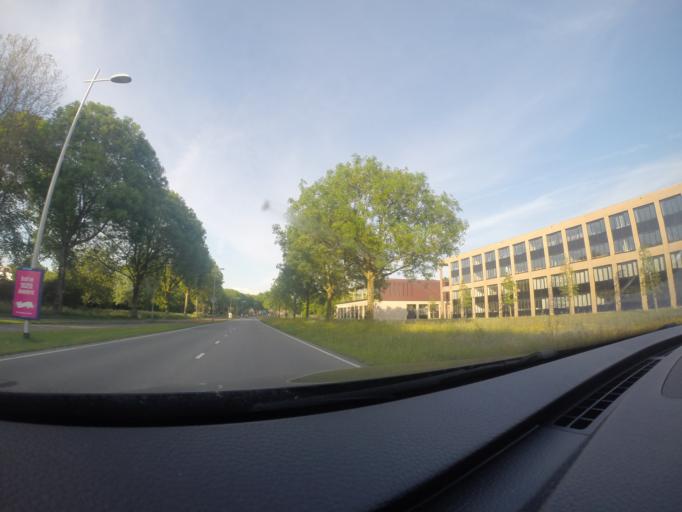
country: NL
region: Overijssel
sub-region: Gemeente Kampen
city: Kampen
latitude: 52.5425
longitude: 5.9215
